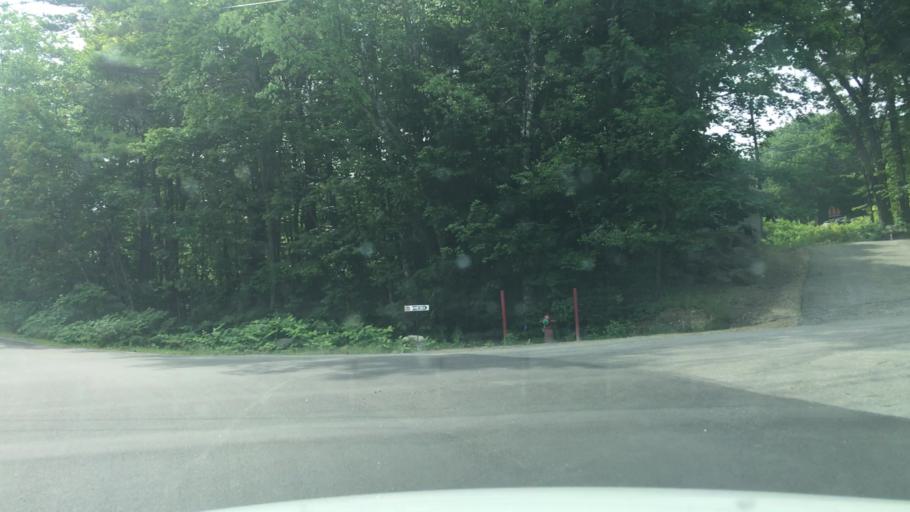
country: US
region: New Hampshire
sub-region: Belknap County
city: Meredith
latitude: 43.6480
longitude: -71.5010
